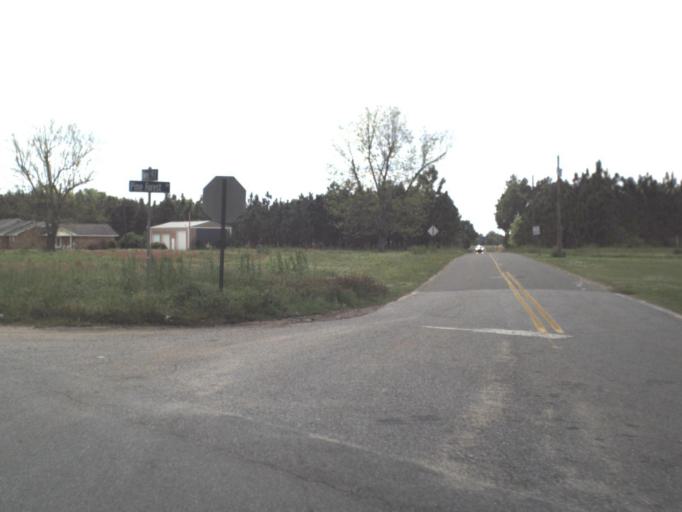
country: US
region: Alabama
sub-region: Escambia County
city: Atmore
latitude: 30.9596
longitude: -87.4855
